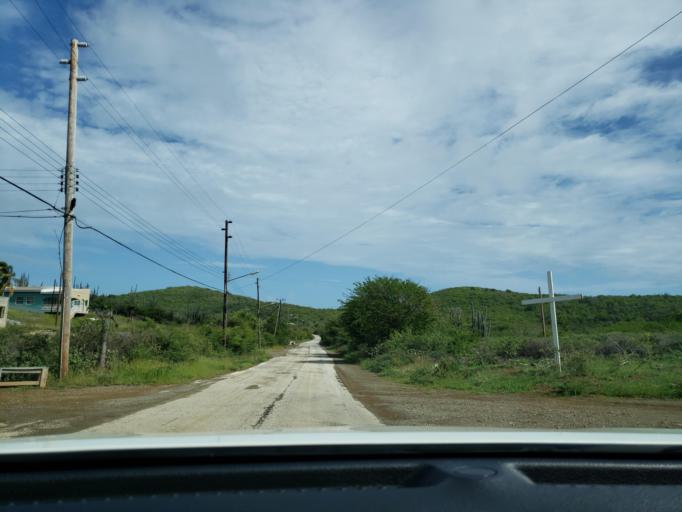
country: CW
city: Barber
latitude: 12.3048
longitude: -69.0915
